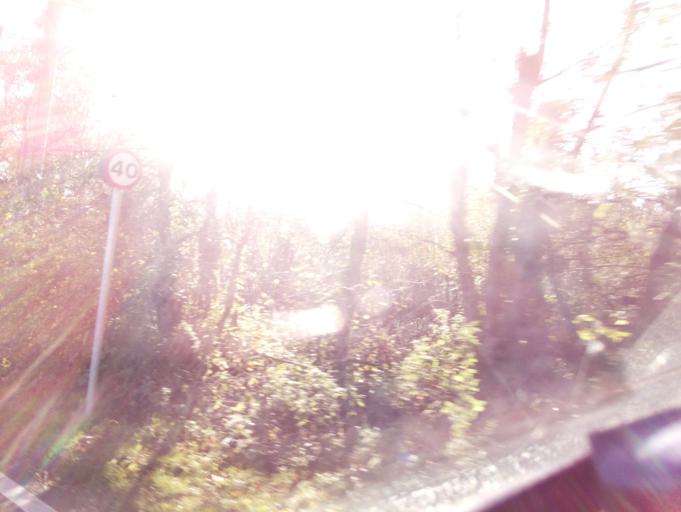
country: GB
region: England
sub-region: Dorset
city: Sherborne
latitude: 50.8677
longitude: -2.4772
